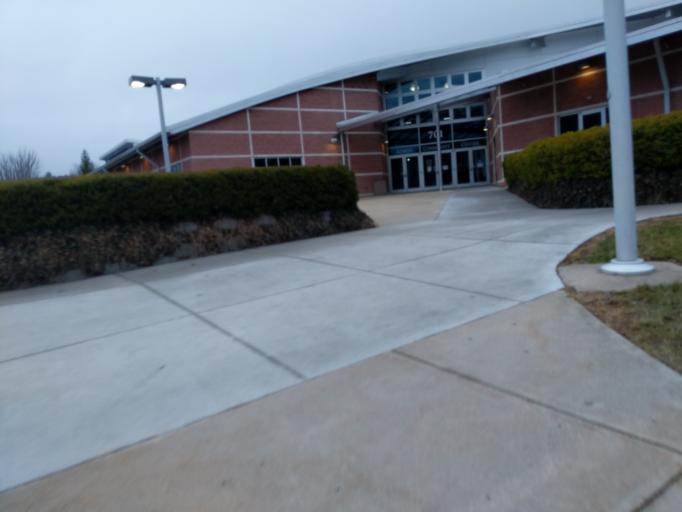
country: US
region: Ohio
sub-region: Athens County
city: Athens
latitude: 39.3369
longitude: -82.0756
